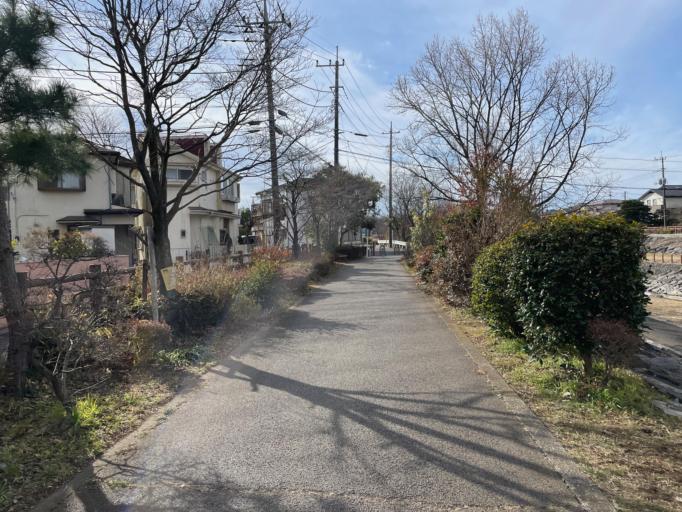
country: JP
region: Saitama
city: Tokorozawa
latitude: 35.7888
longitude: 139.5144
